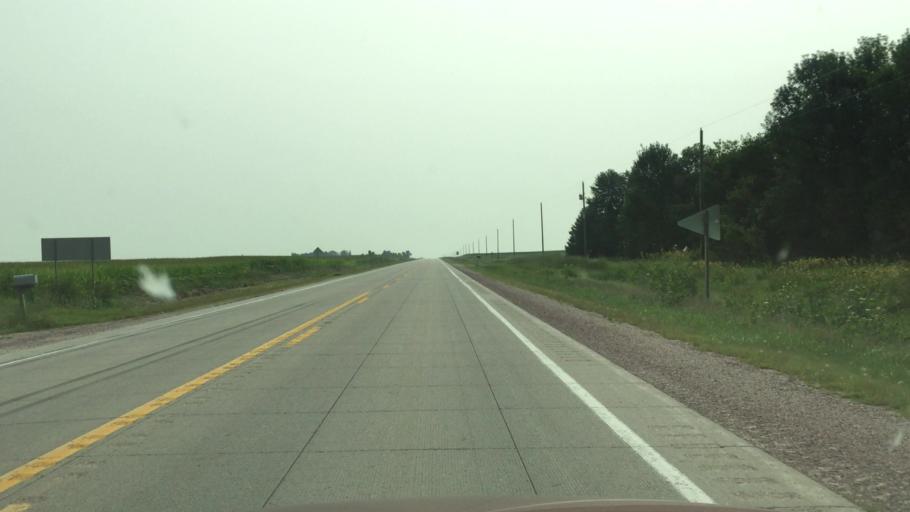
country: US
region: Iowa
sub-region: Osceola County
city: Sibley
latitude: 43.4328
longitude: -95.6412
